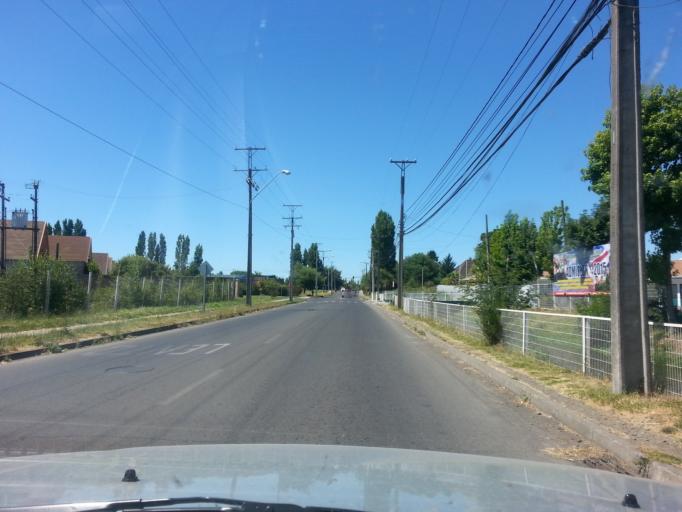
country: CL
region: Biobio
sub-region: Provincia de Nuble
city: Chillan
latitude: -36.5925
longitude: -72.0707
